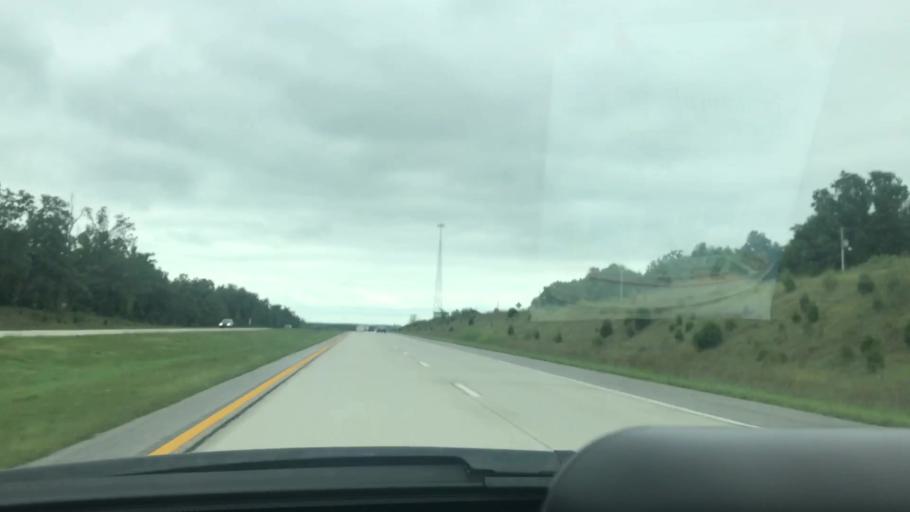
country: US
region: Missouri
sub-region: Greene County
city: Fair Grove
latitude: 37.5040
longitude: -93.1389
